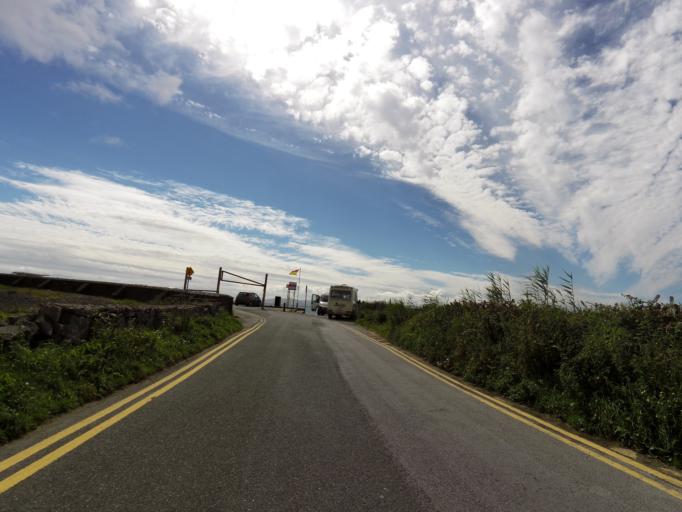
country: IE
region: Connaught
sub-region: County Galway
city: Bearna
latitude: 53.2518
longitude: -9.1284
